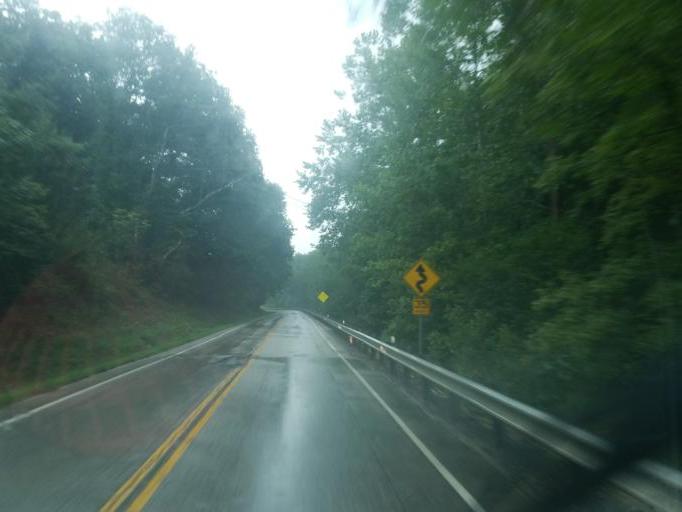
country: US
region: Kentucky
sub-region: Rowan County
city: Morehead
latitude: 38.2685
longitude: -83.3277
